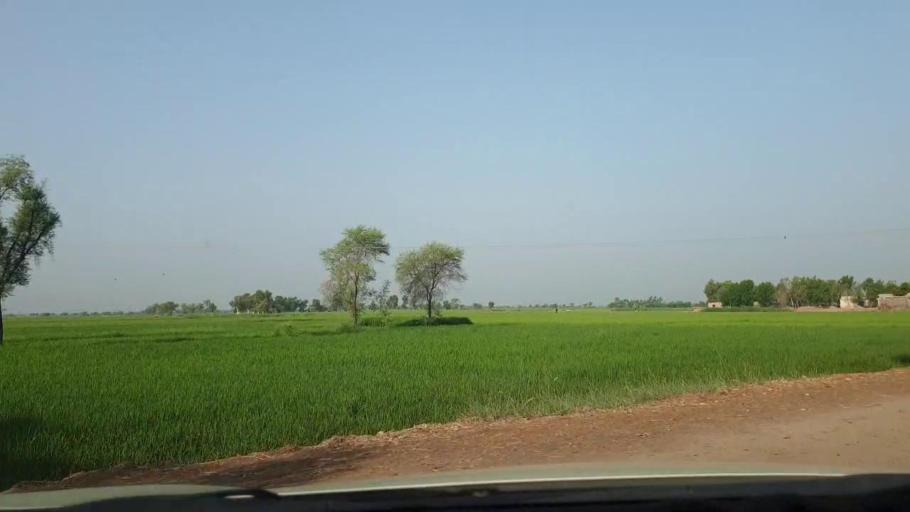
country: PK
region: Sindh
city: Goth Garelo
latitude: 27.4854
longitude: 68.1161
